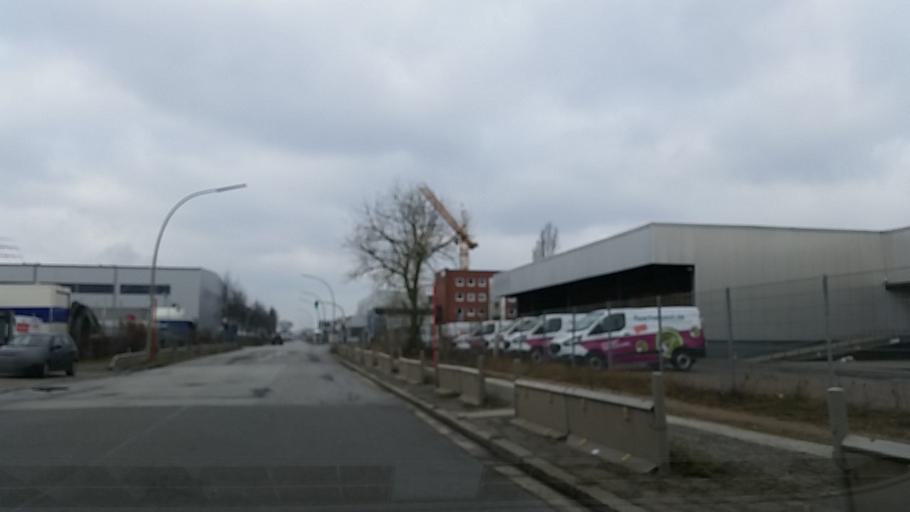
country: DE
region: Hamburg
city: Wandsbek
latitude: 53.5295
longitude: 10.0962
